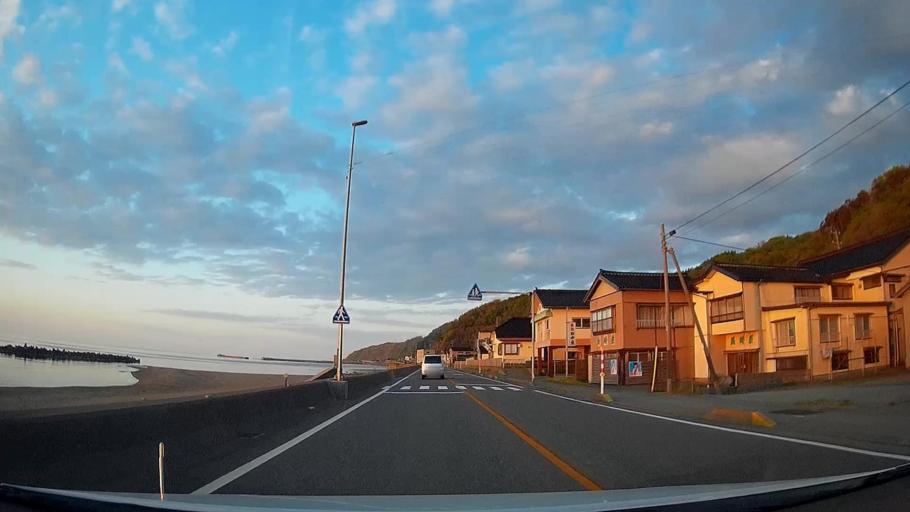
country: JP
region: Niigata
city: Joetsu
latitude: 37.1221
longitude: 138.0392
